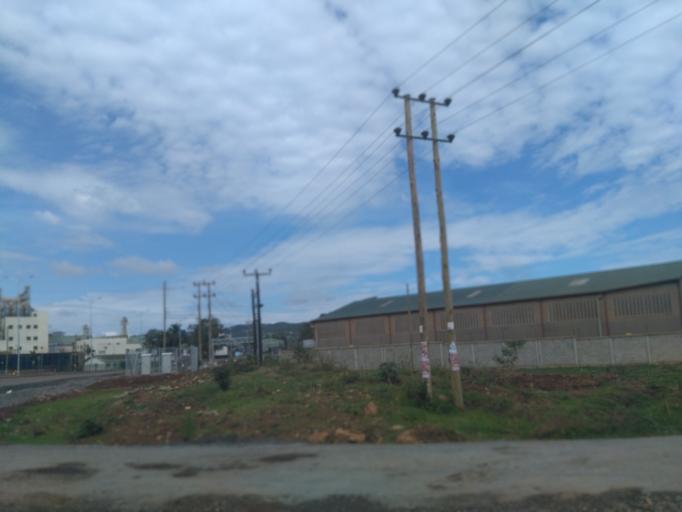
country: UG
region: Eastern Region
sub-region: Jinja District
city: Jinja
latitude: 0.4385
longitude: 33.1839
